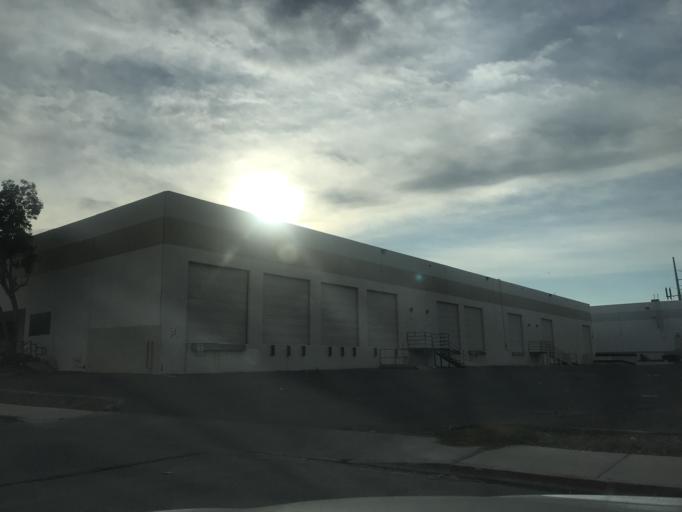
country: US
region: Nevada
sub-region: Clark County
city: Paradise
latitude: 36.1064
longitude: -115.1877
